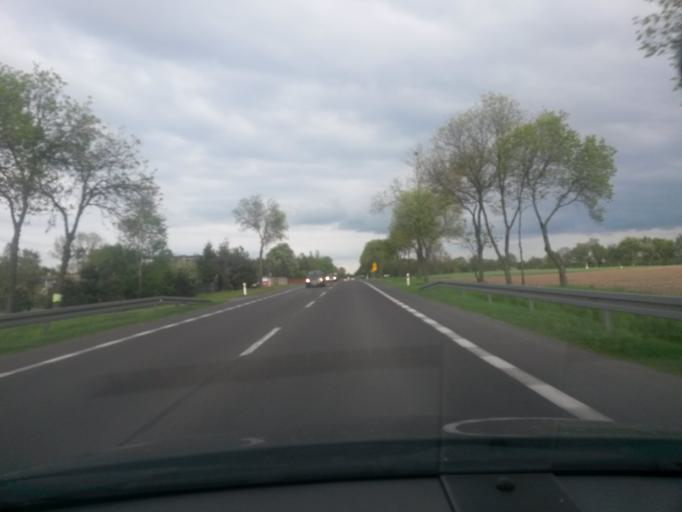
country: PL
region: Masovian Voivodeship
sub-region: Powiat plonski
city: Plonsk
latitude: 52.6199
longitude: 20.3125
